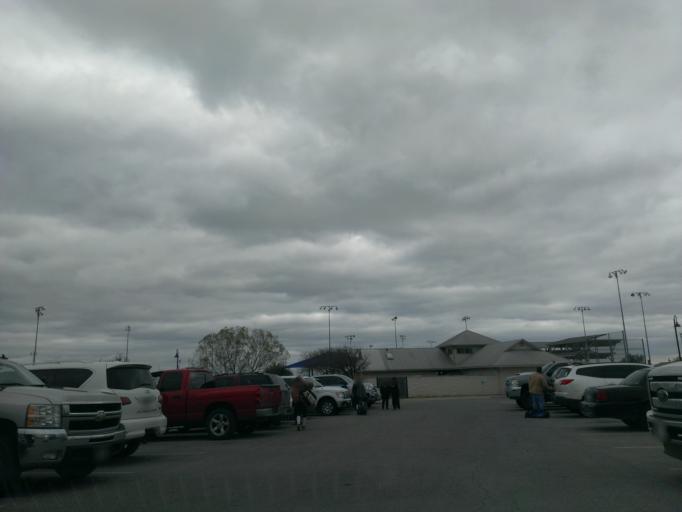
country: US
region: Texas
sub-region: Williamson County
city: Round Rock
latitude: 30.5441
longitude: -97.6242
